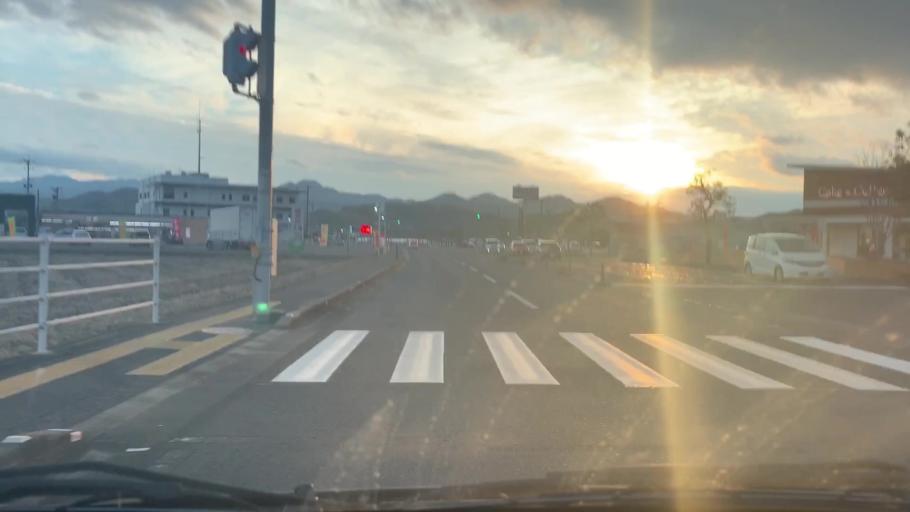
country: JP
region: Saga Prefecture
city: Kashima
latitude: 33.1201
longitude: 130.0923
